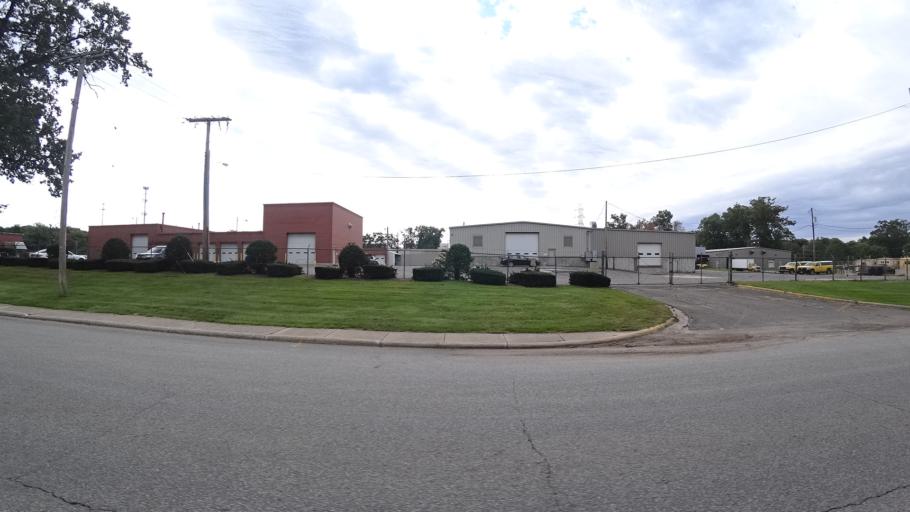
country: US
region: Indiana
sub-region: LaPorte County
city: Trail Creek
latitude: 41.7021
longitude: -86.8764
